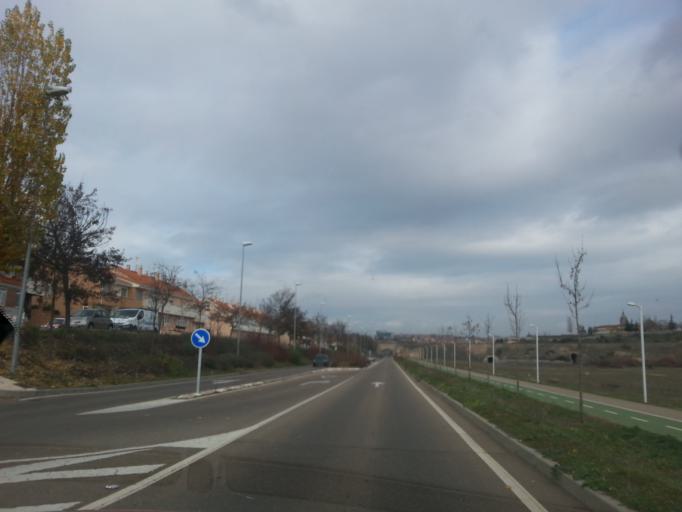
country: ES
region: Castille and Leon
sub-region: Provincia de Salamanca
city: Salamanca
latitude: 40.9486
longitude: -5.6779
